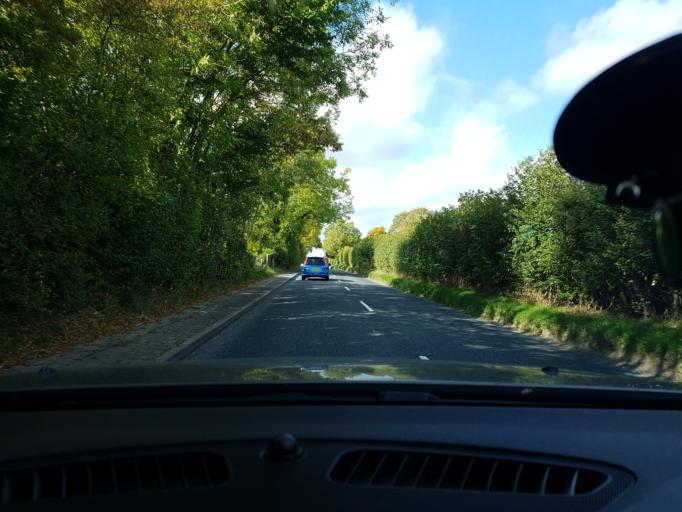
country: GB
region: England
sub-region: Wiltshire
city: Aldbourne
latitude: 51.4727
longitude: -1.6125
